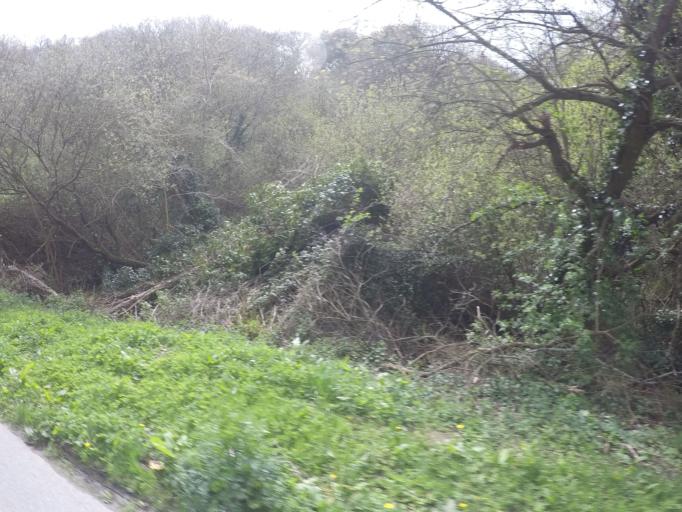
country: FR
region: Brittany
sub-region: Departement des Cotes-d'Armor
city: Plouezec
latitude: 48.7321
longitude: -2.9527
